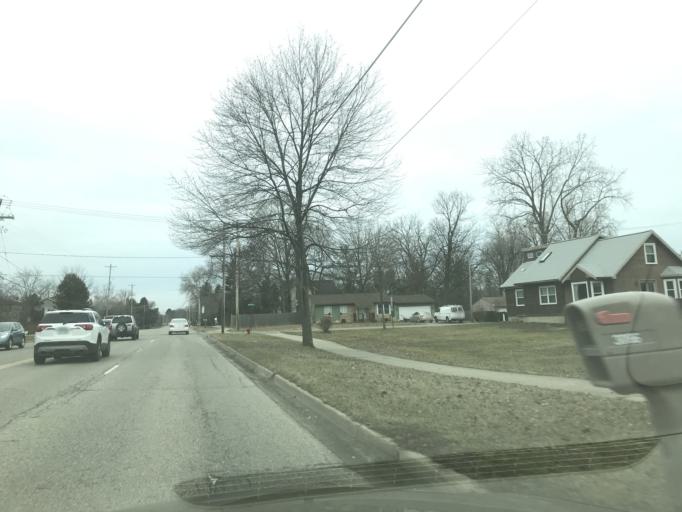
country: US
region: Michigan
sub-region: Ingham County
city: East Lansing
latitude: 42.7552
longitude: -84.4666
